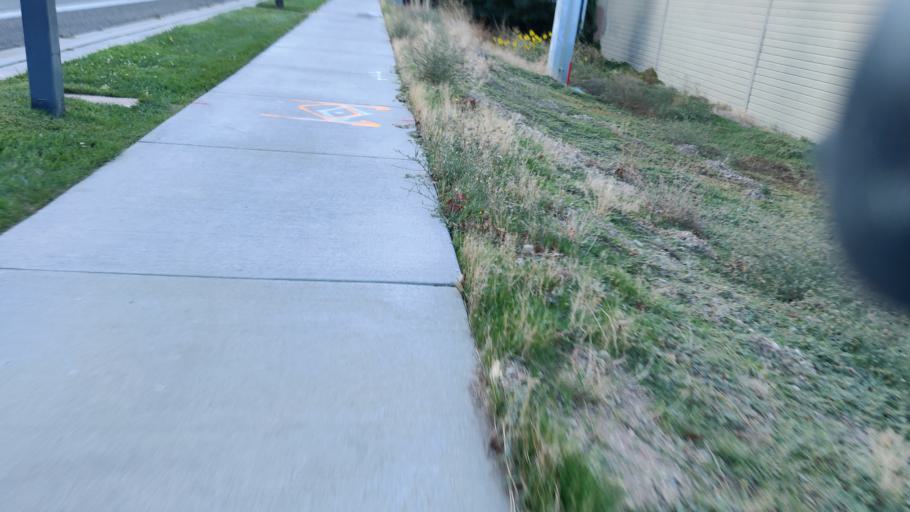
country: US
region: Idaho
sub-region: Ada County
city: Boise
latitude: 43.6064
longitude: -116.1895
